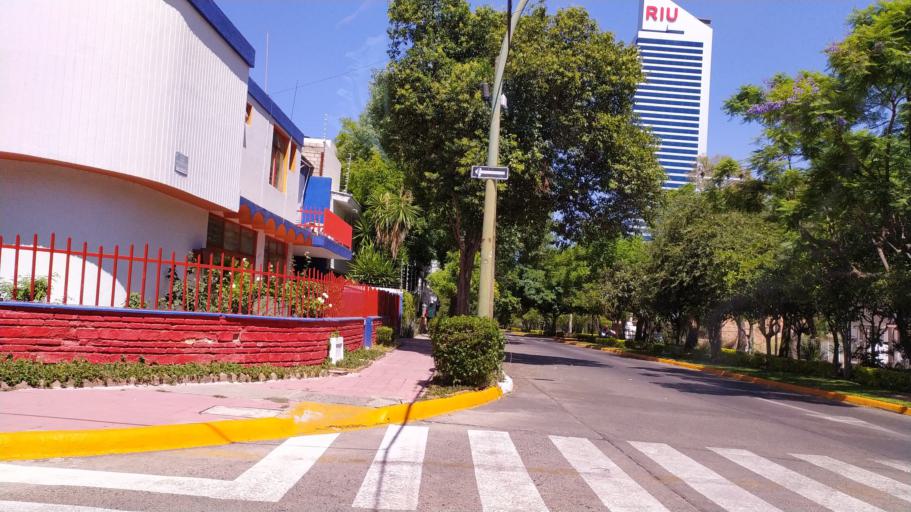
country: MX
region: Jalisco
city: Guadalajara
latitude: 20.6685
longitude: -103.3960
